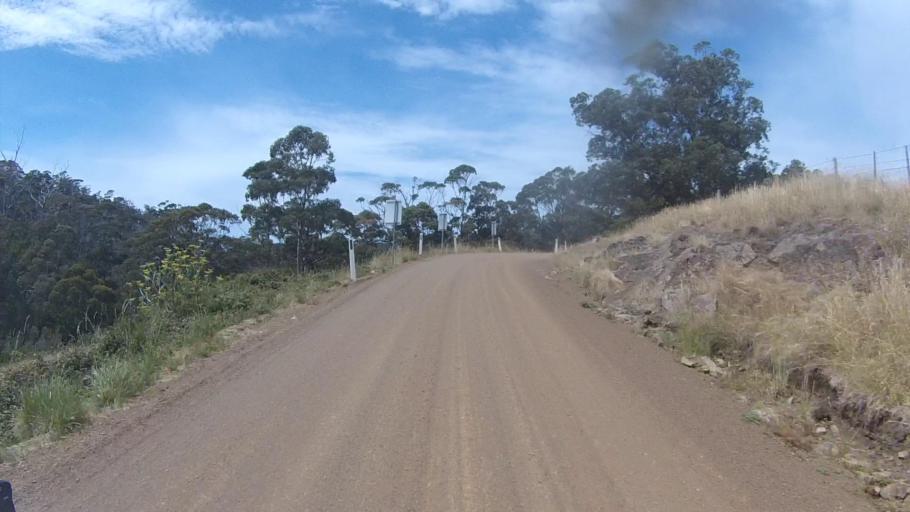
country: AU
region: Tasmania
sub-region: Sorell
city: Sorell
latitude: -42.7881
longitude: 147.8421
